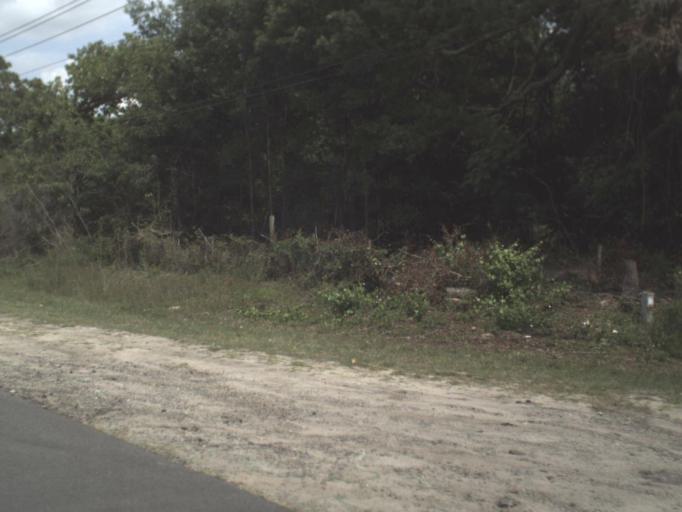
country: US
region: Florida
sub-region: Putnam County
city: Interlachen
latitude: 29.6136
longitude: -81.9832
